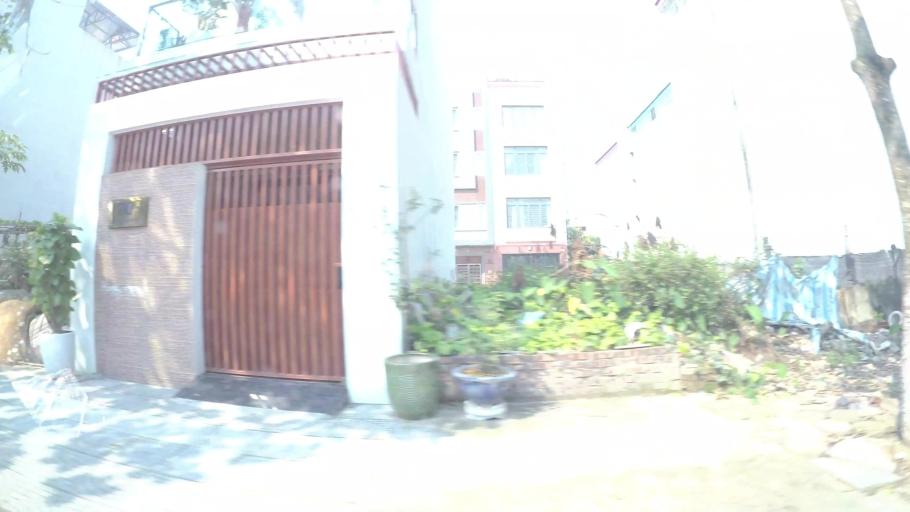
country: VN
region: Ha Noi
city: Ha Dong
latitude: 20.9553
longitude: 105.8060
